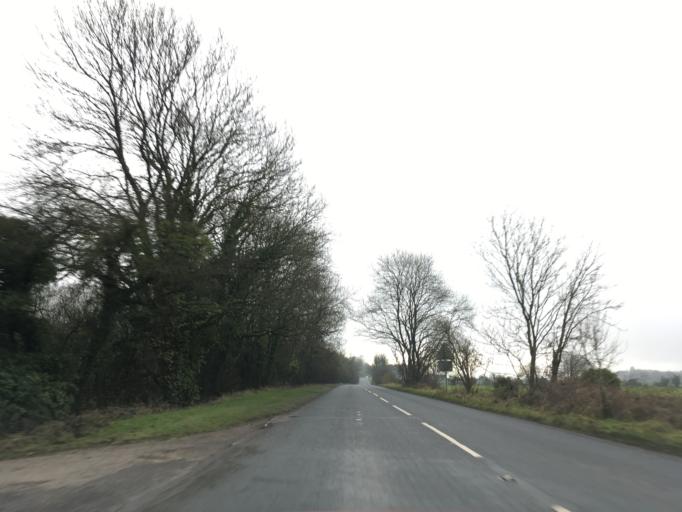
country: GB
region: England
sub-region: Gloucestershire
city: Nailsworth
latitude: 51.6365
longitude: -2.2508
